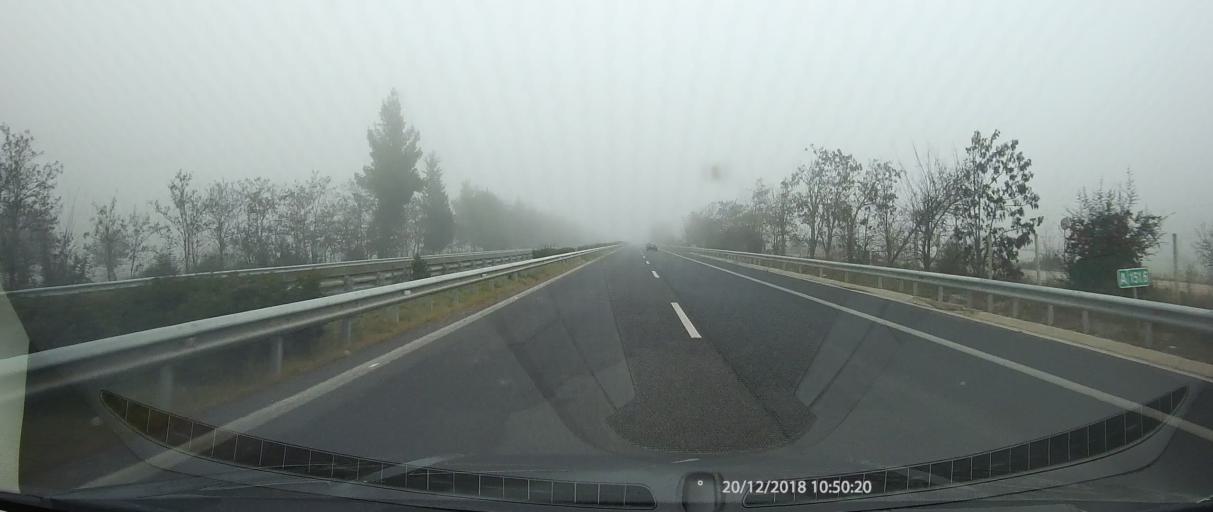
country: GR
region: Peloponnese
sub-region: Nomos Arkadias
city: Tripoli
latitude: 37.5607
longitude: 22.4237
